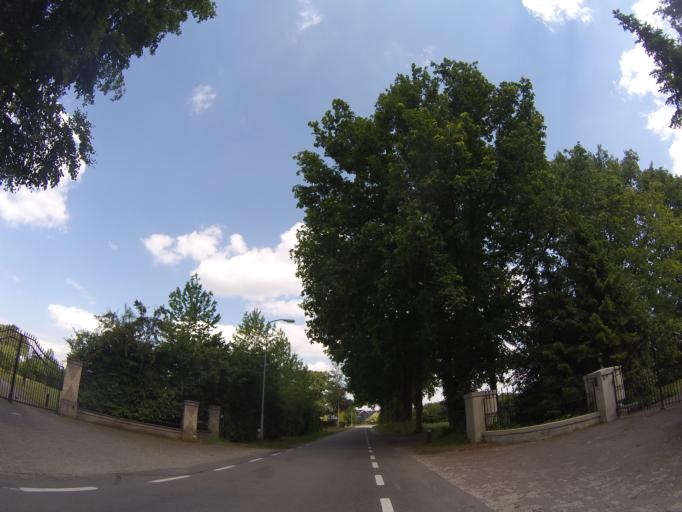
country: NL
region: Gelderland
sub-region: Gemeente Barneveld
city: Voorthuizen
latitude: 52.2038
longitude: 5.6385
